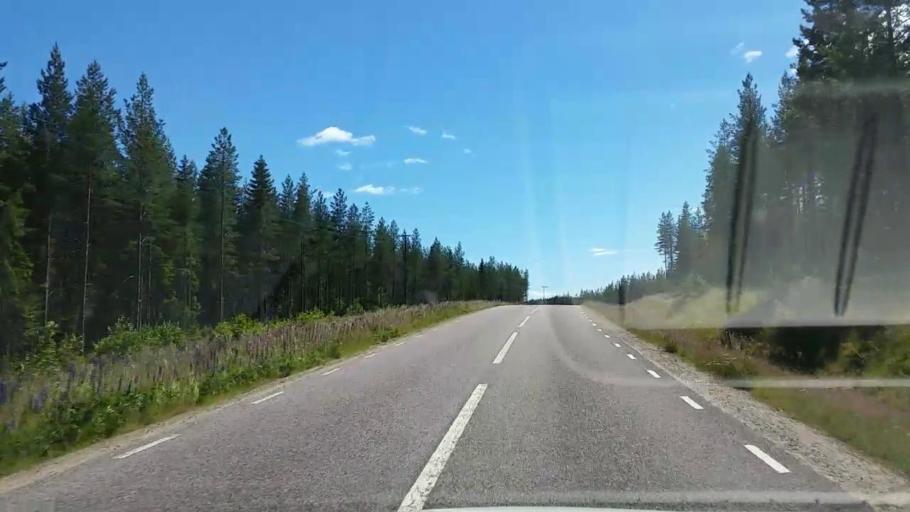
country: SE
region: Gaevleborg
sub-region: Ovanakers Kommun
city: Edsbyn
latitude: 61.5734
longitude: 15.6668
